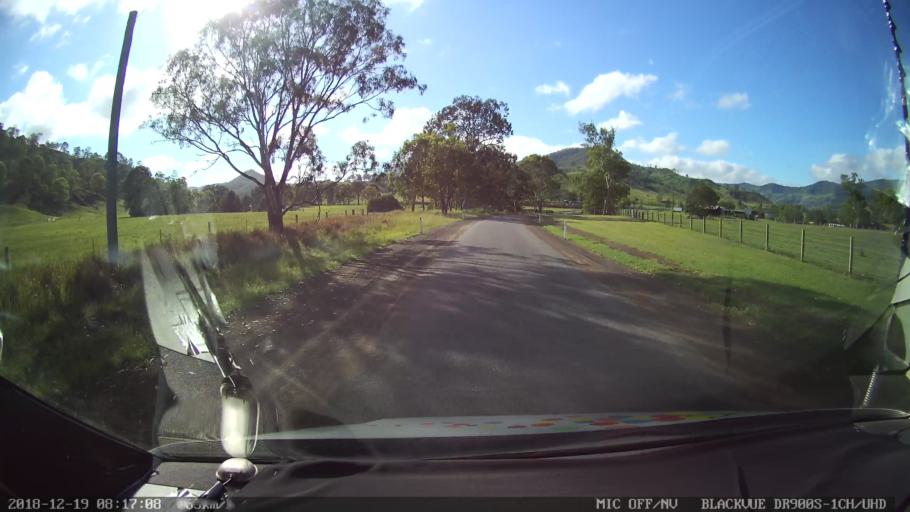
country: AU
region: New South Wales
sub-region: Kyogle
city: Kyogle
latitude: -28.2629
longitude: 152.9092
